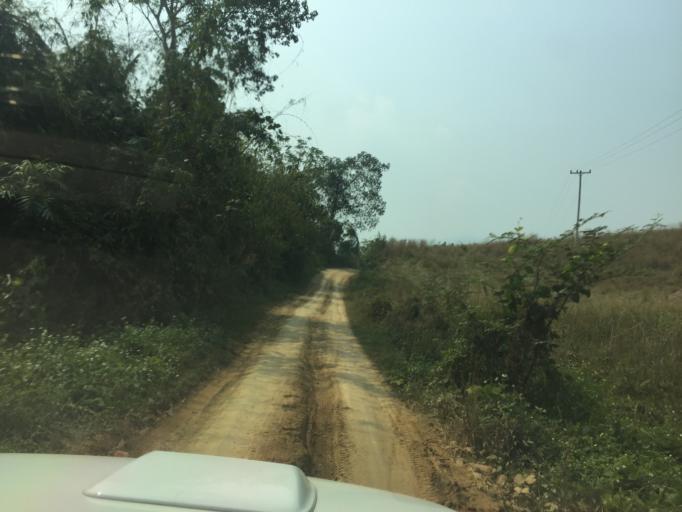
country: TH
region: Phayao
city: Phu Sang
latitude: 19.5890
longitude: 100.5259
